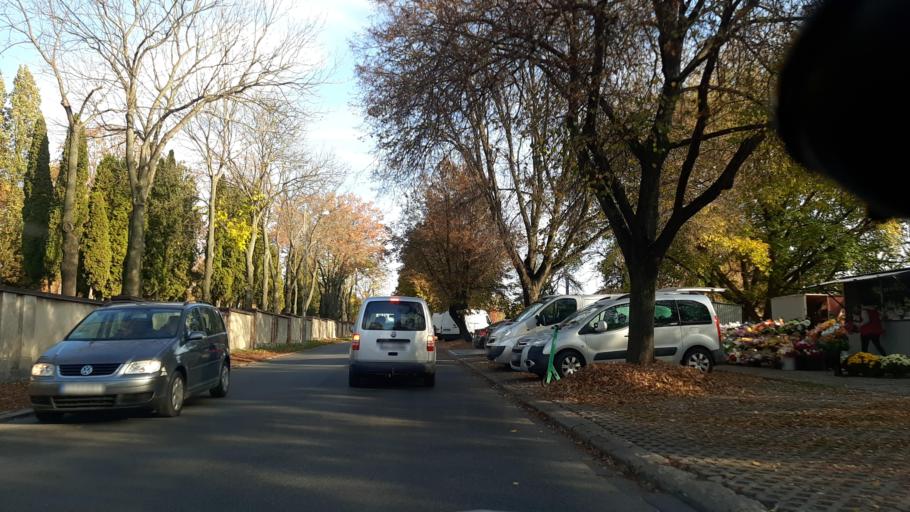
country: PL
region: Lublin Voivodeship
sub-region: Powiat lubelski
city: Lublin
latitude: 51.2606
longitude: 22.5800
